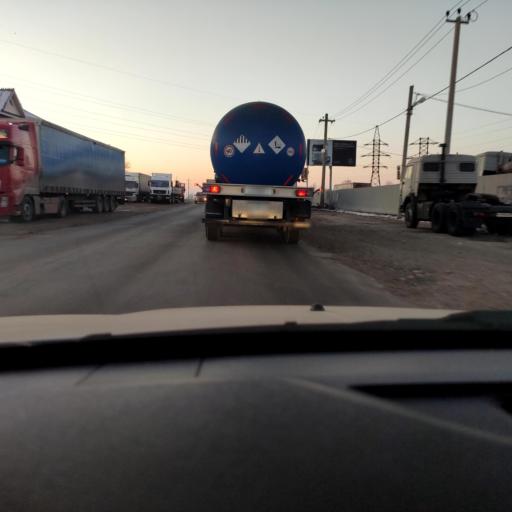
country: RU
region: Samara
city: Smyshlyayevka
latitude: 53.2508
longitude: 50.4749
